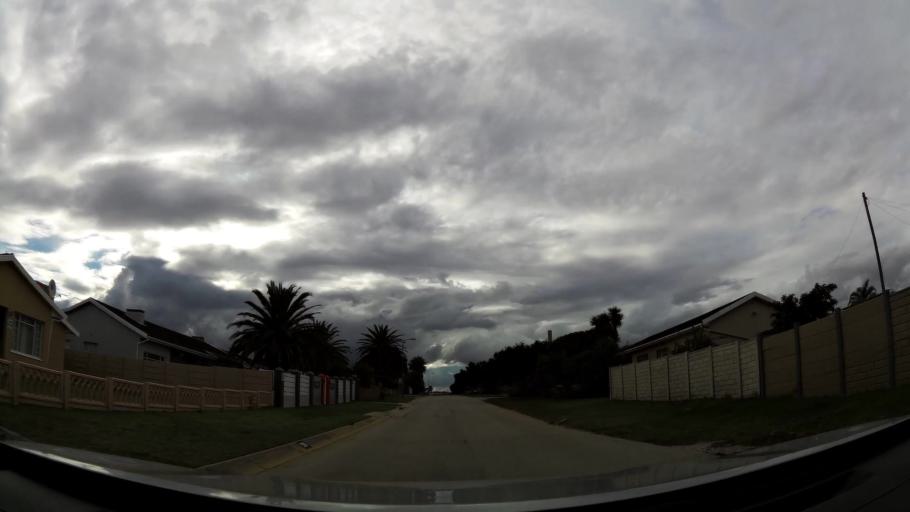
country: ZA
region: Eastern Cape
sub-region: Nelson Mandela Bay Metropolitan Municipality
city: Port Elizabeth
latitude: -33.9411
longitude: 25.4747
